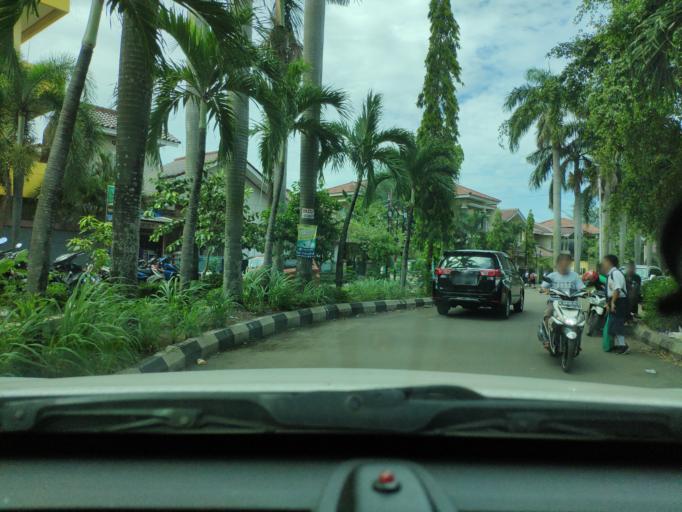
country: ID
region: West Java
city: Ciputat
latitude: -6.2216
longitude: 106.7078
